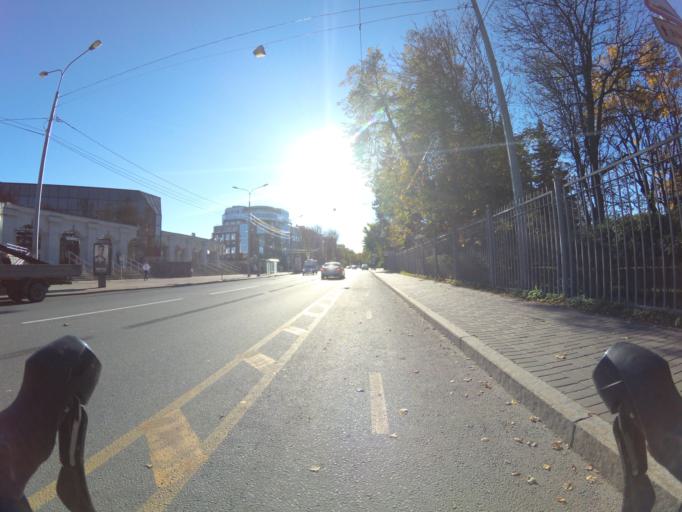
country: RU
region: Leningrad
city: Krestovskiy ostrov
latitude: 59.9722
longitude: 30.2586
